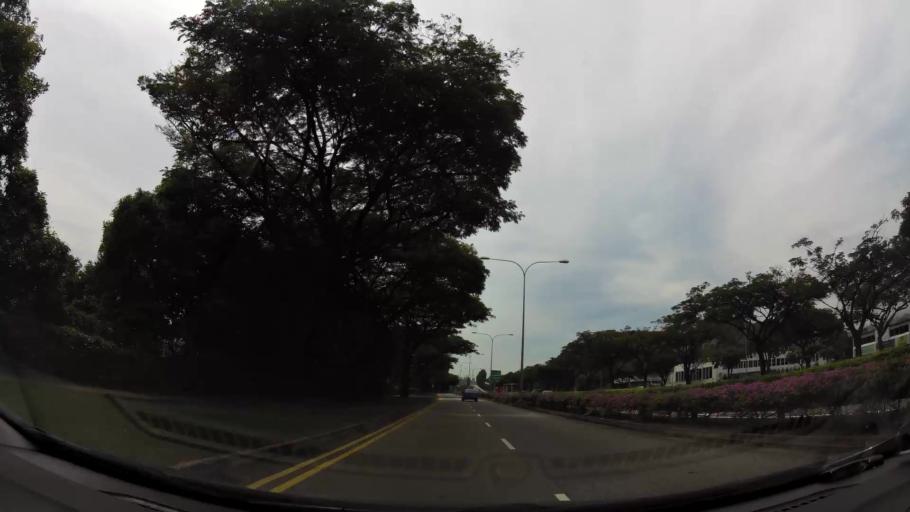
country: MY
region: Johor
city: Johor Bahru
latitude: 1.3225
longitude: 103.6847
